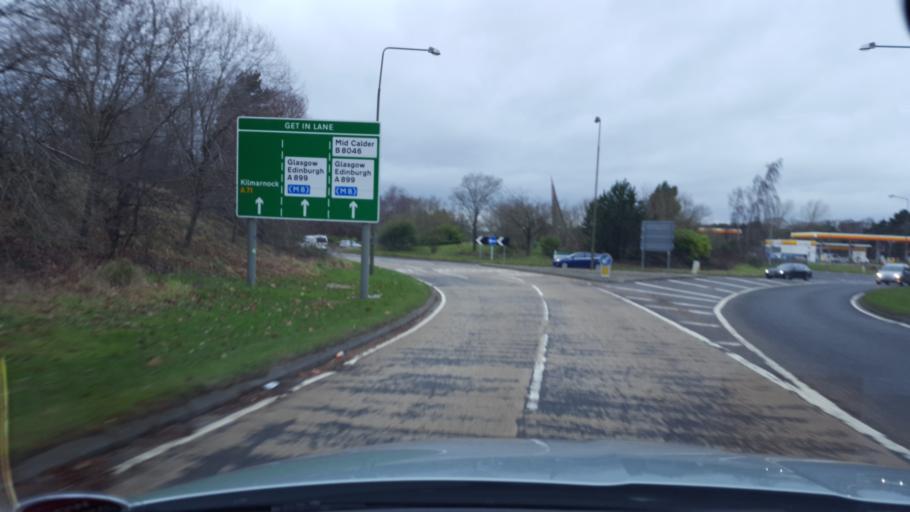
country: GB
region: Scotland
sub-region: West Lothian
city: Mid Calder
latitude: 55.8798
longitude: -3.4909
